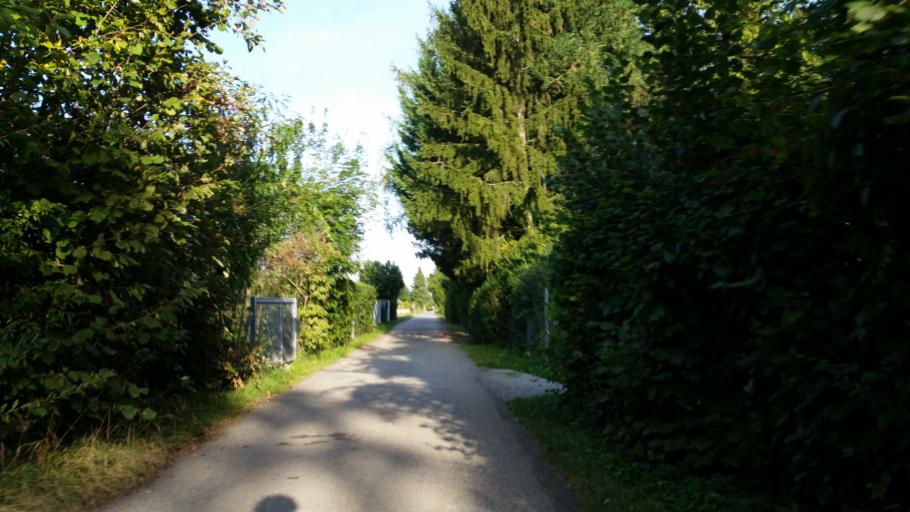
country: DE
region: Baden-Wuerttemberg
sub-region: Regierungsbezirk Stuttgart
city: Ludwigsburg
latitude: 48.8835
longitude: 9.2192
